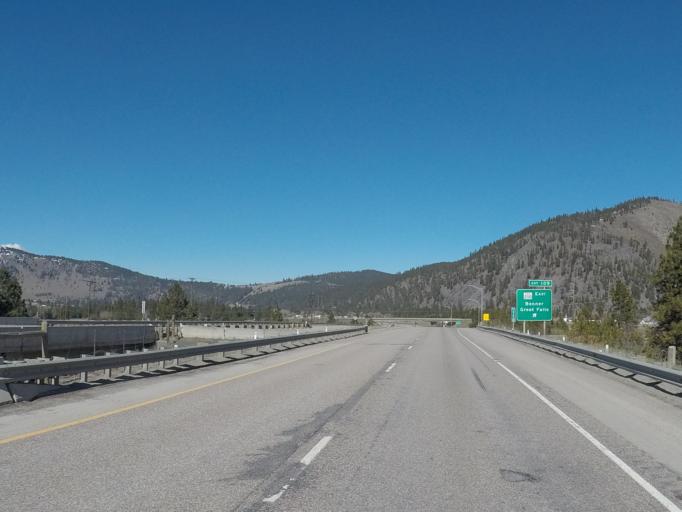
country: US
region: Montana
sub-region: Missoula County
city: Bonner-West Riverside
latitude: 46.8738
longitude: -113.8894
